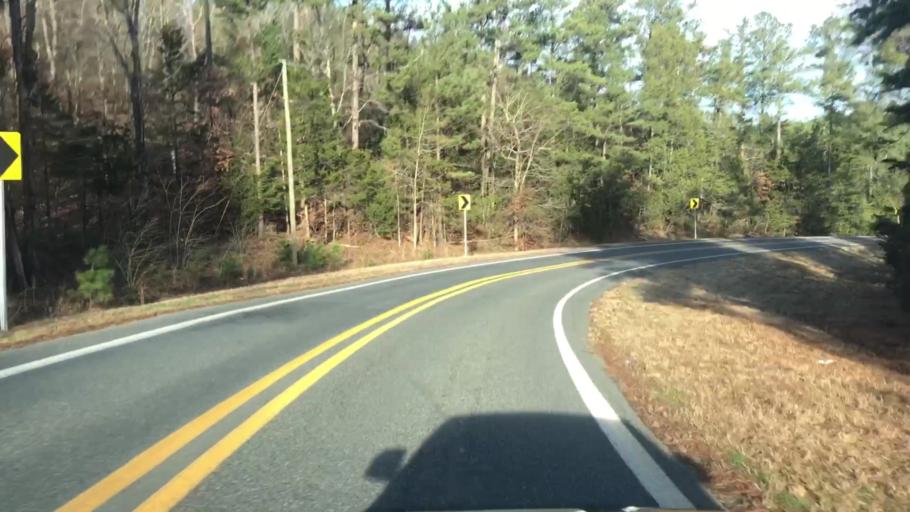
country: US
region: Arkansas
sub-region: Garland County
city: Rockwell
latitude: 34.4886
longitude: -93.2757
